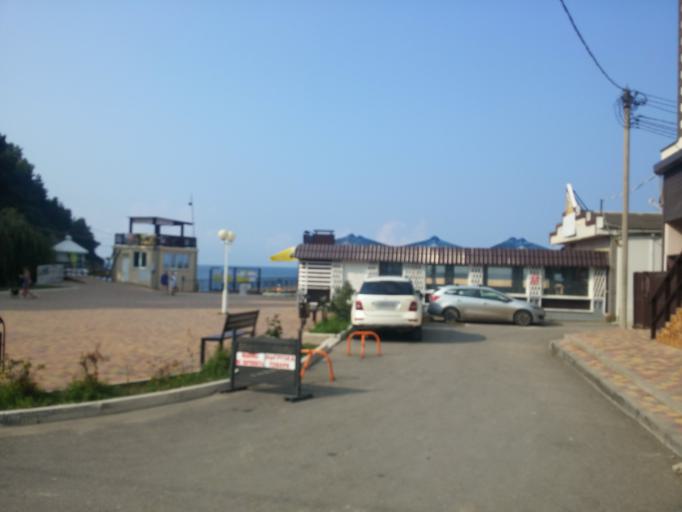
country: RU
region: Krasnodarskiy
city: Divnomorskoye
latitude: 44.4628
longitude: 38.1522
